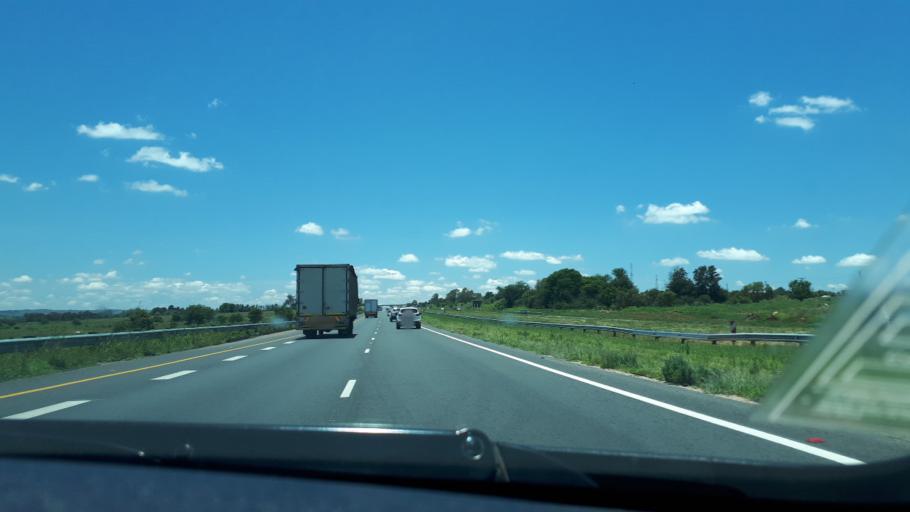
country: ZA
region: Gauteng
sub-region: City of Johannesburg Metropolitan Municipality
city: Diepsloot
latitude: -25.9797
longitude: 27.9305
